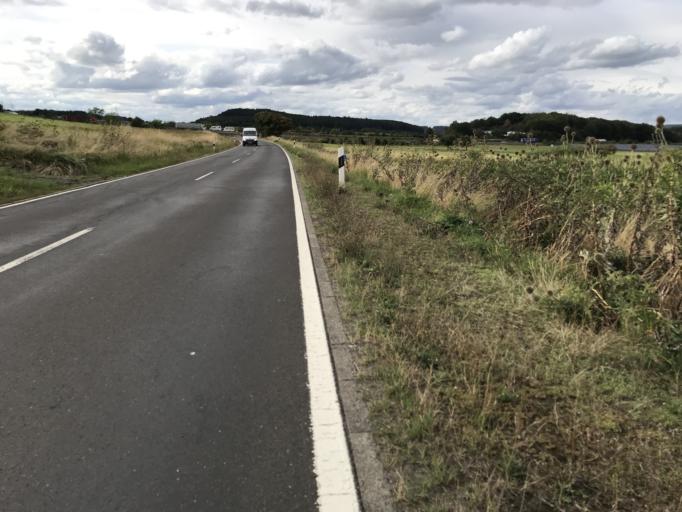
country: DE
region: Hesse
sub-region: Regierungsbezirk Giessen
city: Reiskirchen
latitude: 50.5811
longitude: 8.8105
